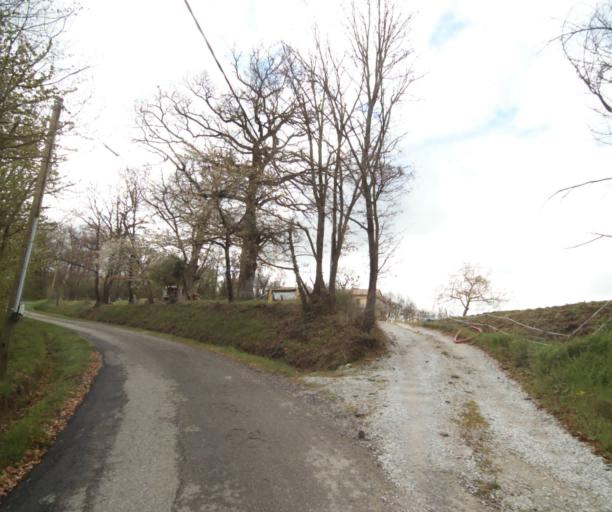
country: FR
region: Midi-Pyrenees
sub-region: Departement de l'Ariege
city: Saverdun
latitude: 43.2147
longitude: 1.5391
